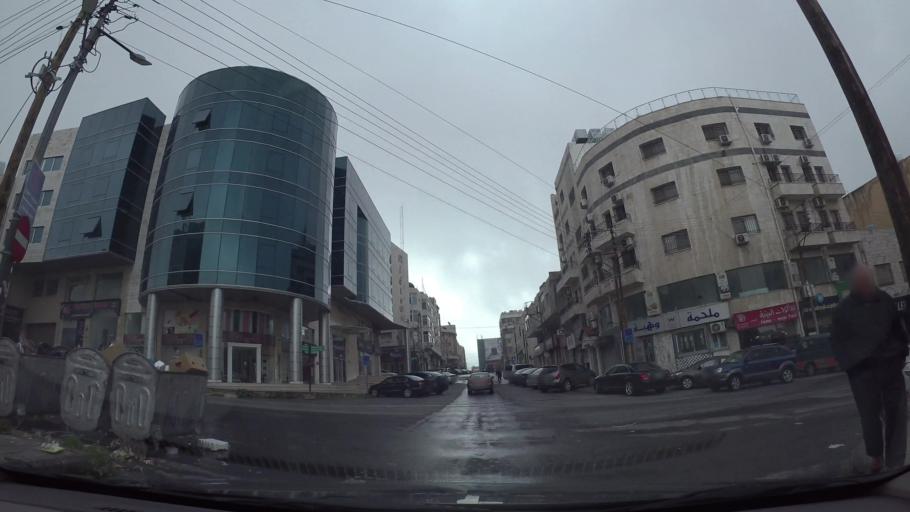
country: JO
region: Amman
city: Wadi as Sir
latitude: 31.9583
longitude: 35.8664
